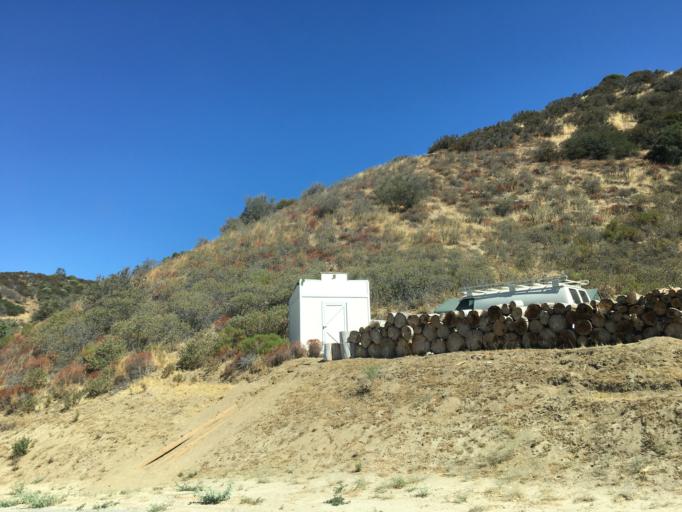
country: US
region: California
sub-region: Los Angeles County
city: Green Valley
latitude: 34.6788
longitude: -118.4464
